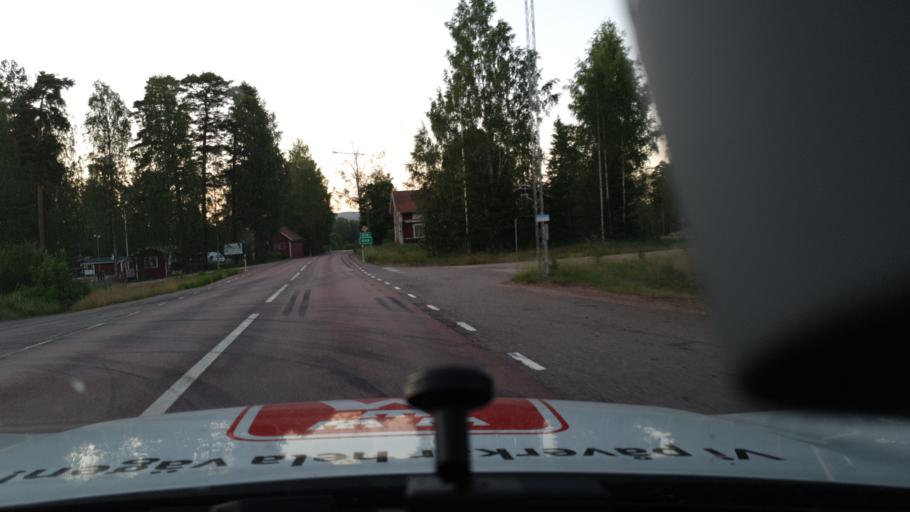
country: SE
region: Vaermland
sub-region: Torsby Kommun
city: Torsby
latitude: 60.2749
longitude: 13.0295
